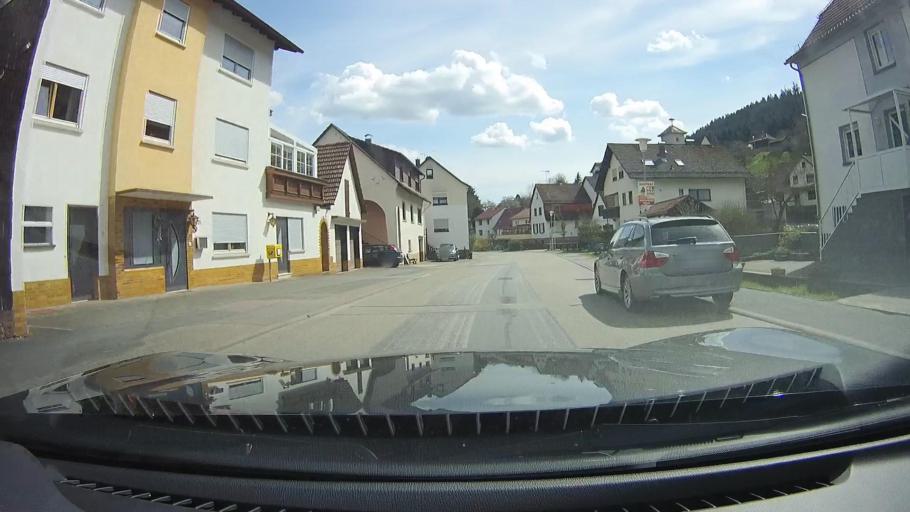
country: DE
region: Hesse
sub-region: Regierungsbezirk Darmstadt
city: Hesseneck
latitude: 49.5684
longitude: 9.0677
